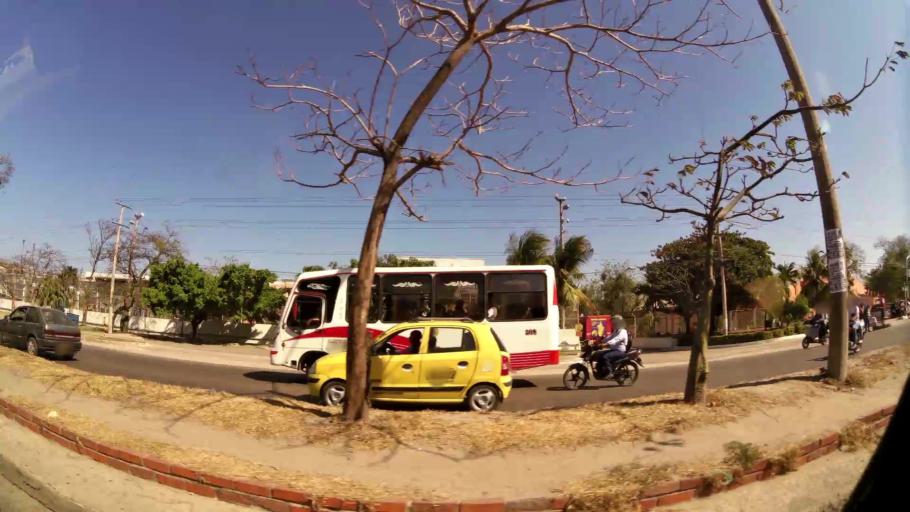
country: CO
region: Atlantico
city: Barranquilla
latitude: 10.9569
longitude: -74.7859
